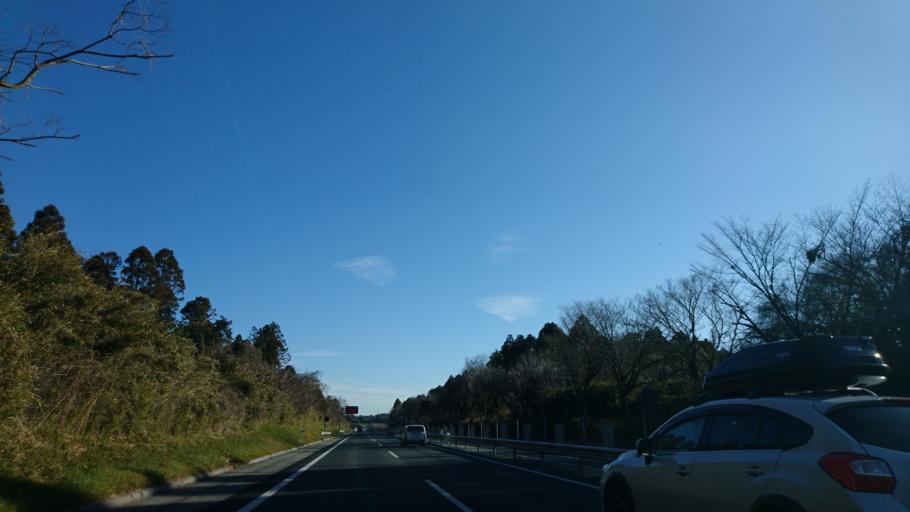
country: JP
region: Chiba
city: Oami
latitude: 35.5697
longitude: 140.2553
